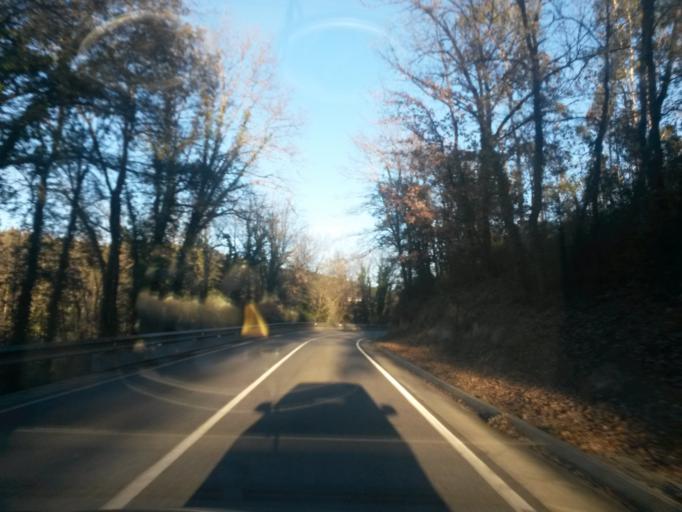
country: ES
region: Catalonia
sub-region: Provincia de Girona
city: Massanes
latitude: 41.7596
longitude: 2.6816
